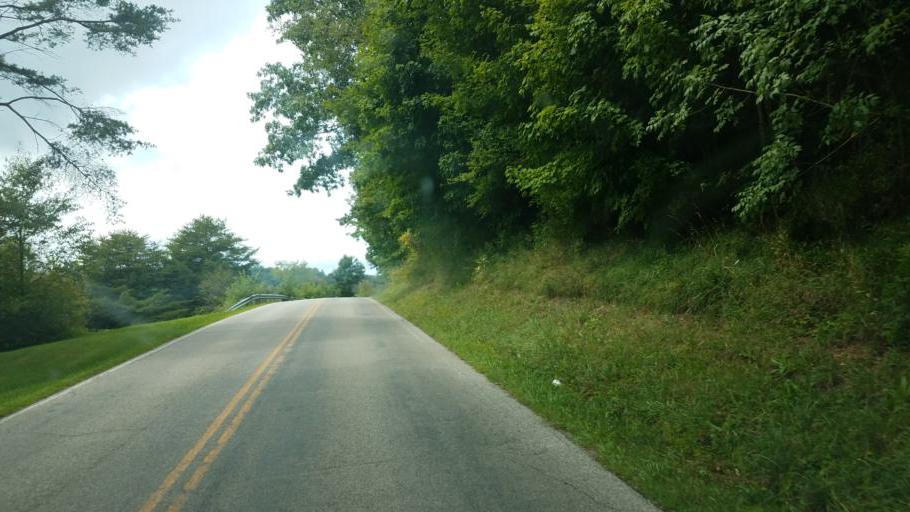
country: US
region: Ohio
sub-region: Sandusky County
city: Bellville
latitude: 40.6622
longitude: -82.4867
